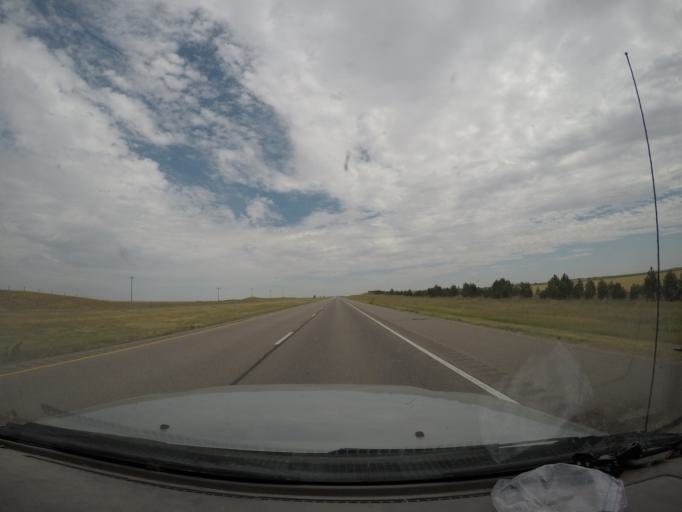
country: US
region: Nebraska
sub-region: Kimball County
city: Kimball
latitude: 41.1958
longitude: -103.7553
